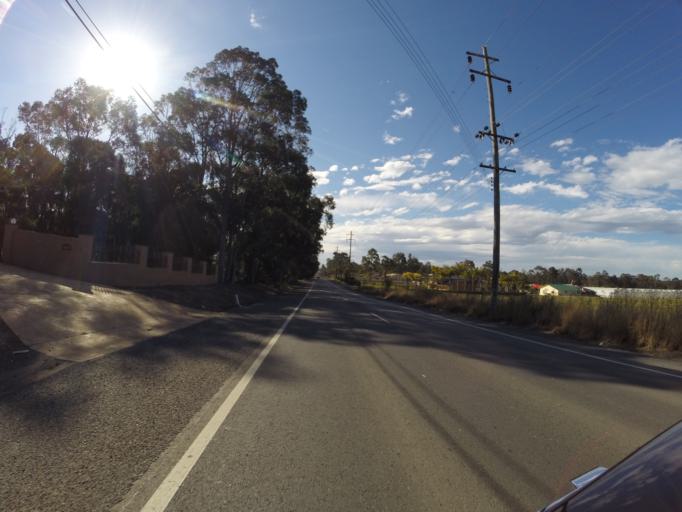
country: AU
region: New South Wales
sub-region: Fairfield
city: Cecil Park
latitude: -33.9008
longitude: 150.7889
